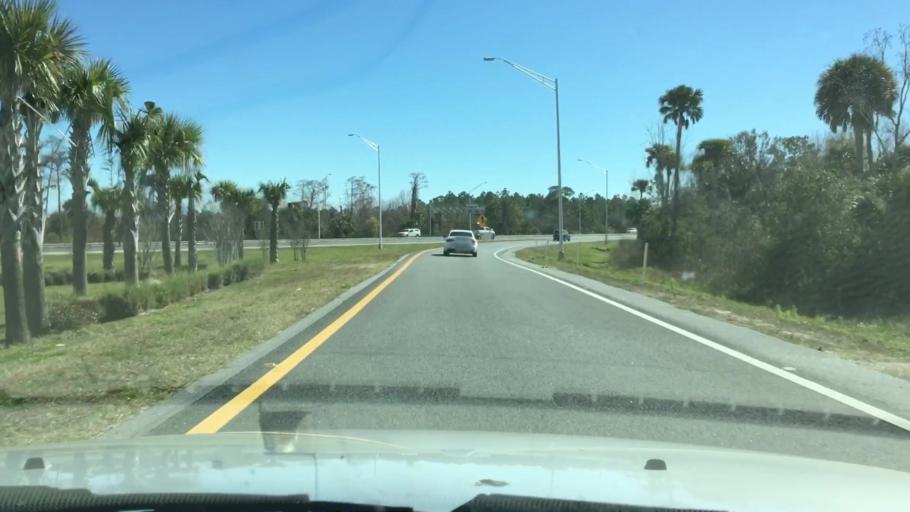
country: US
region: Florida
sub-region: Flagler County
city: Palm Coast
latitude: 29.5973
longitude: -81.2477
